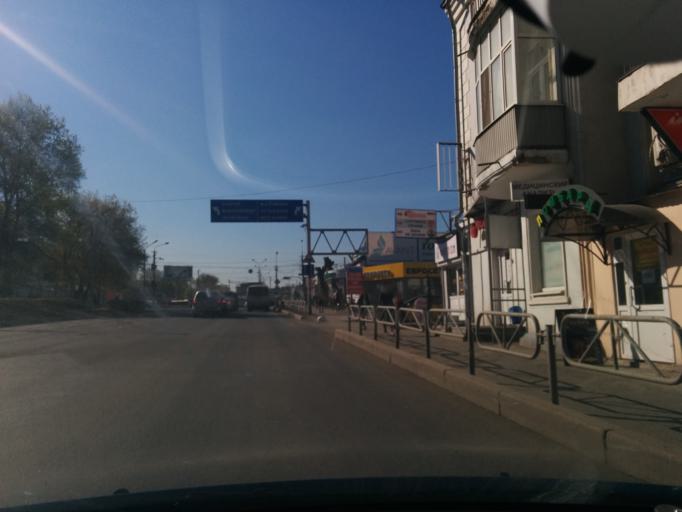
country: RU
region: Perm
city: Perm
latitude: 58.0047
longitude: 56.2297
